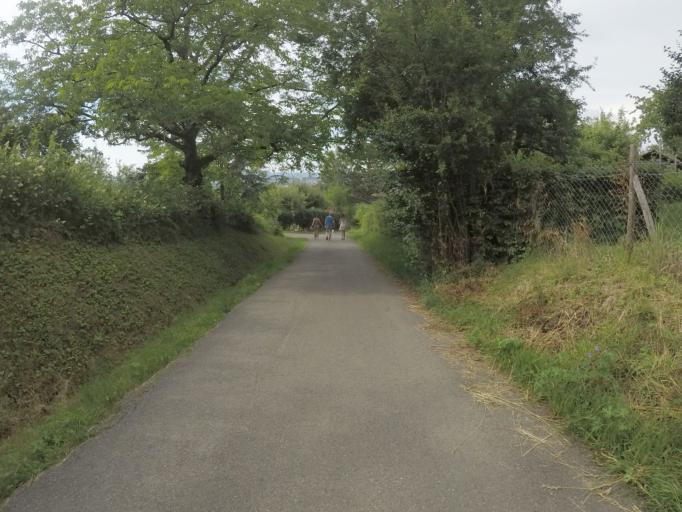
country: DE
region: Baden-Wuerttemberg
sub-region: Tuebingen Region
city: Pfullingen
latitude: 48.4740
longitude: 9.2163
